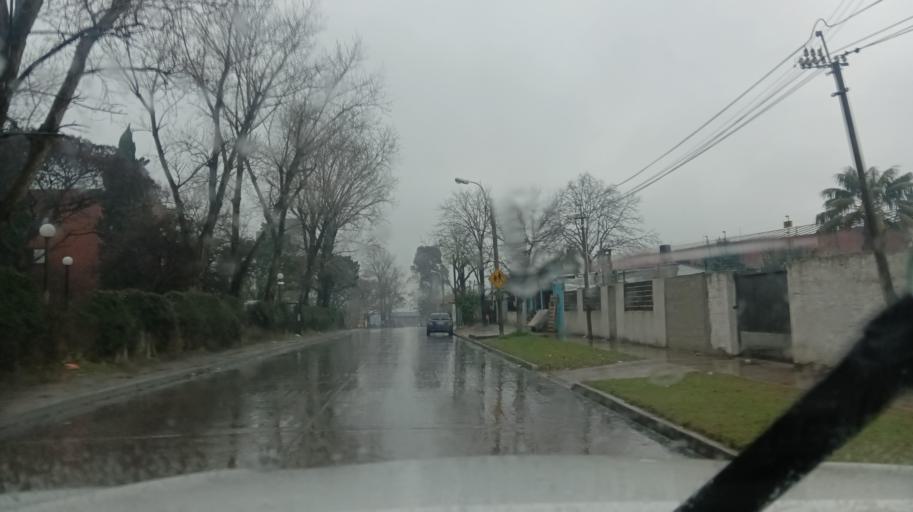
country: UY
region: Canelones
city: Paso de Carrasco
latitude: -34.8737
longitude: -56.1224
